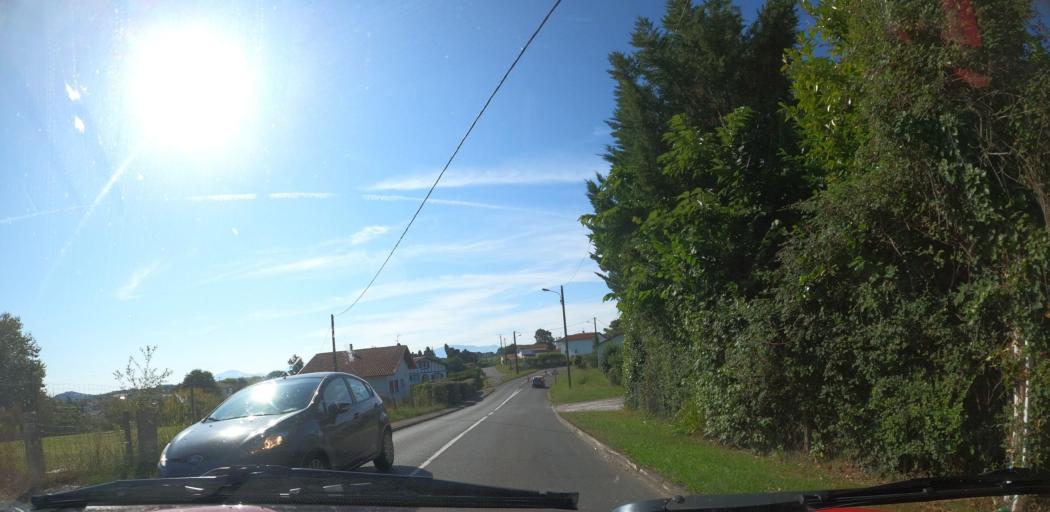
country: FR
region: Aquitaine
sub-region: Departement des Pyrenees-Atlantiques
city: Arbonne
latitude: 43.4222
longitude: -1.5480
